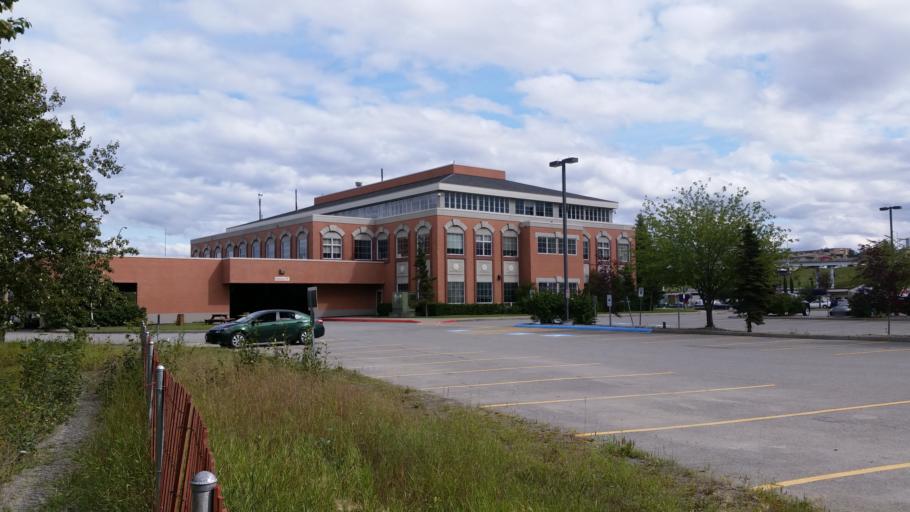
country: US
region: Alaska
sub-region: Anchorage Municipality
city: Anchorage
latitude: 61.2230
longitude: -149.8898
